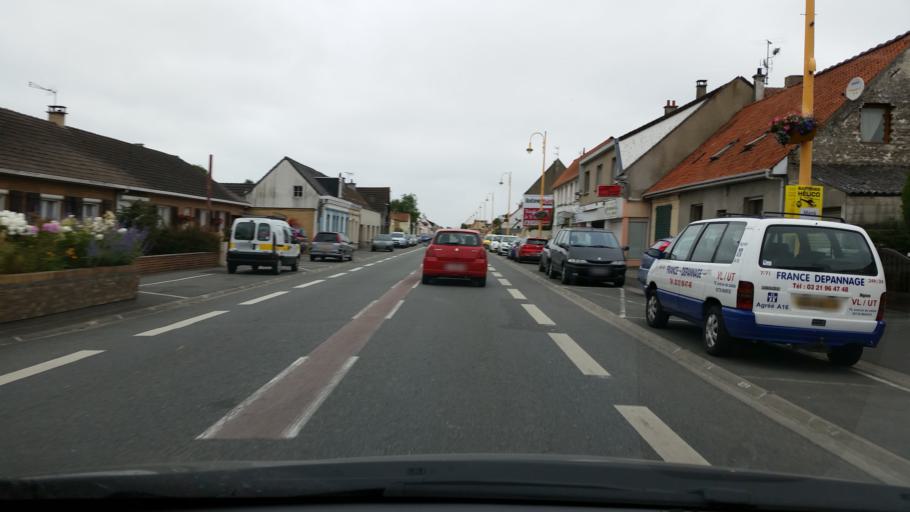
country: FR
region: Nord-Pas-de-Calais
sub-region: Departement du Pas-de-Calais
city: Marck
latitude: 50.9478
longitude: 1.9494
